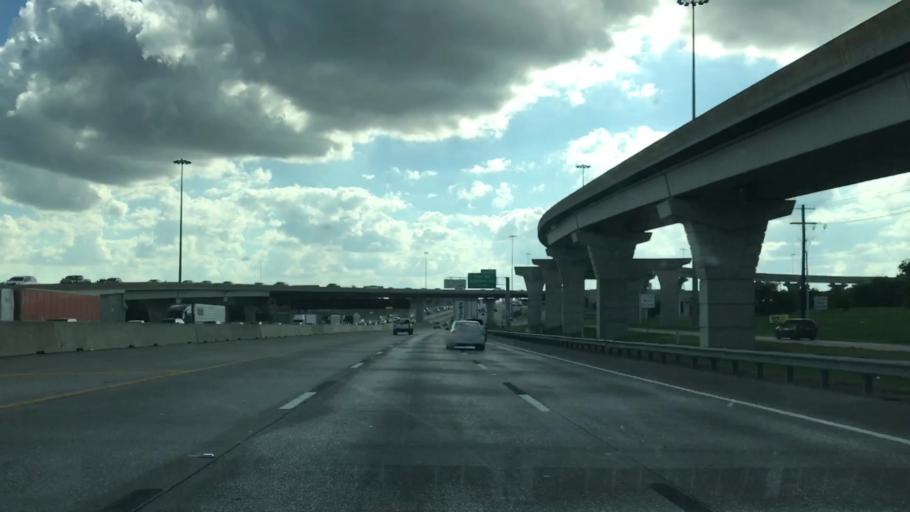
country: US
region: Texas
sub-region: Dallas County
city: Rowlett
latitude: 32.8607
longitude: -96.5493
